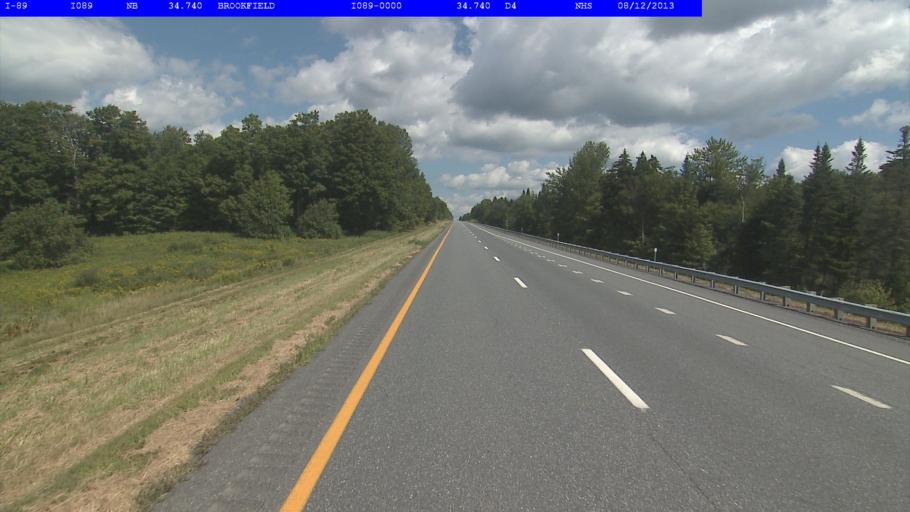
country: US
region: Vermont
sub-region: Orange County
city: Randolph
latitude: 43.9996
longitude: -72.6224
